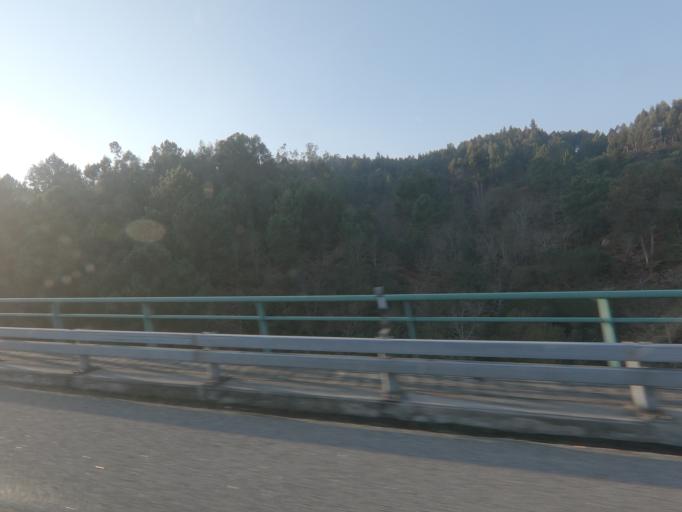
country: PT
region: Porto
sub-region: Amarante
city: Amarante
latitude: 41.2344
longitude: -8.1220
